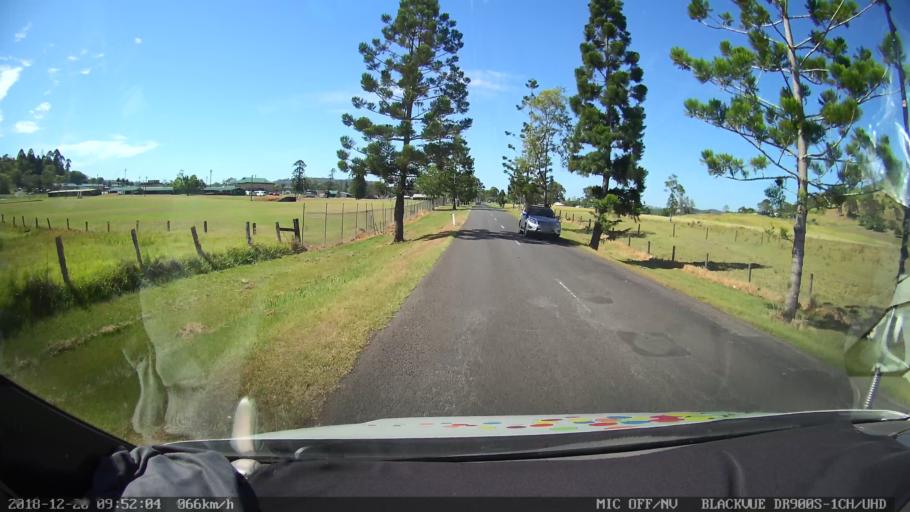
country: AU
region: New South Wales
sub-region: Lismore Municipality
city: Lismore
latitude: -28.7927
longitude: 153.2723
